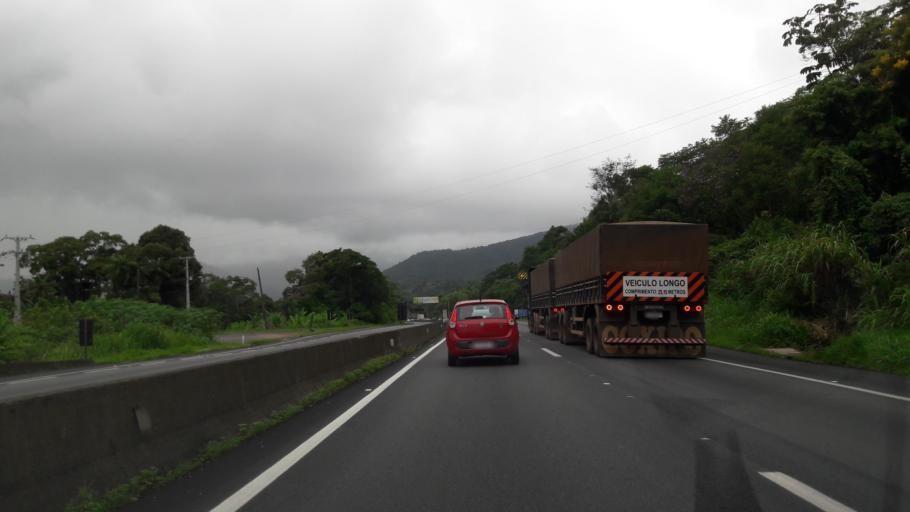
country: BR
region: Parana
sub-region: Antonina
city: Antonina
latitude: -25.5717
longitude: -48.8362
